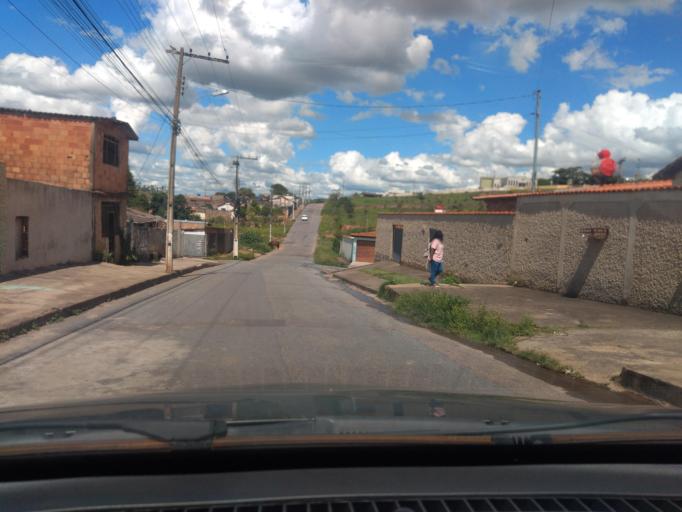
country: BR
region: Minas Gerais
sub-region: Tres Coracoes
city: Tres Coracoes
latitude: -21.6828
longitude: -45.2470
